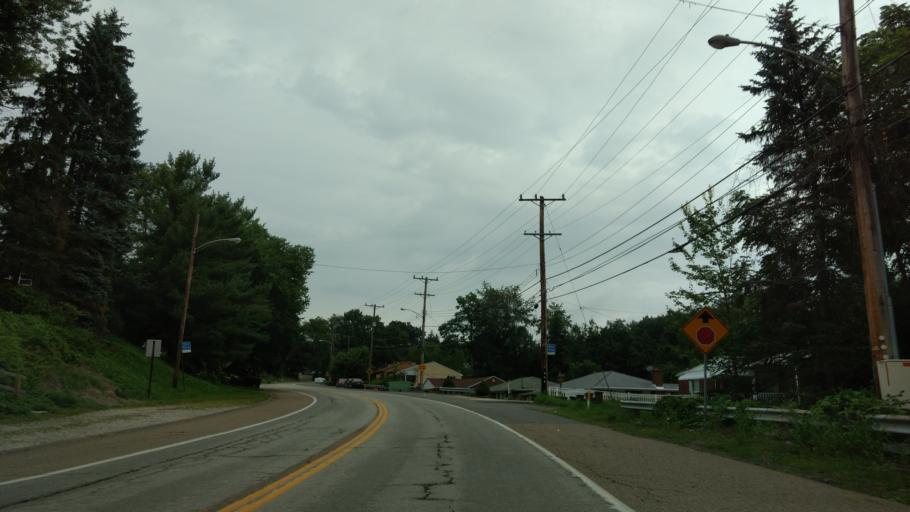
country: US
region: Pennsylvania
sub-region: Allegheny County
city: West View
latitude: 40.5116
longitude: -80.0454
